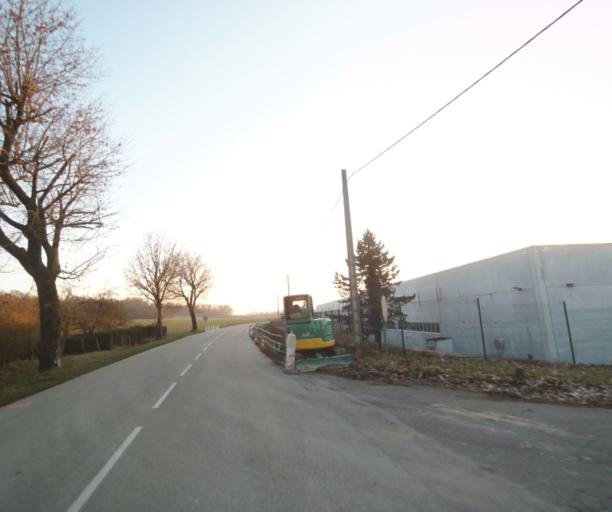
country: FR
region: Champagne-Ardenne
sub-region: Departement de la Haute-Marne
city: Bienville
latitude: 48.5976
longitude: 5.0431
